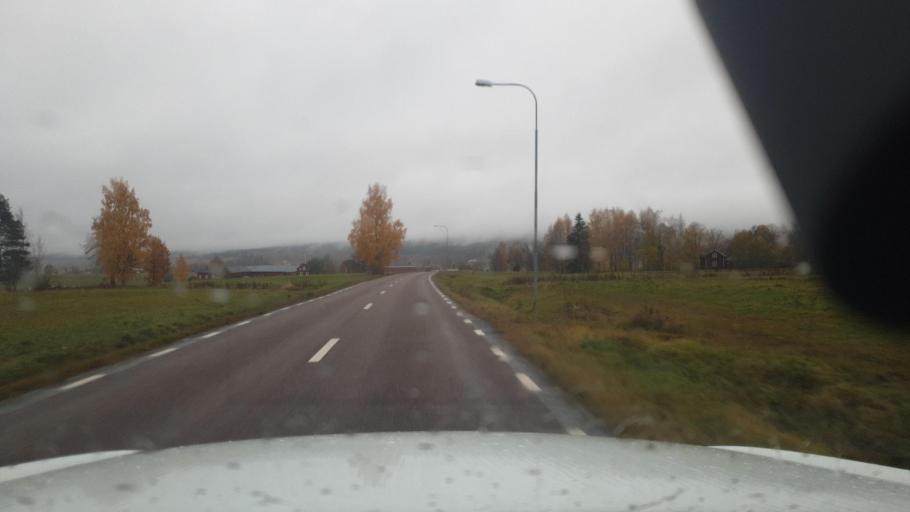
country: SE
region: Vaermland
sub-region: Sunne Kommun
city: Sunne
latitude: 59.8600
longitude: 12.9456
